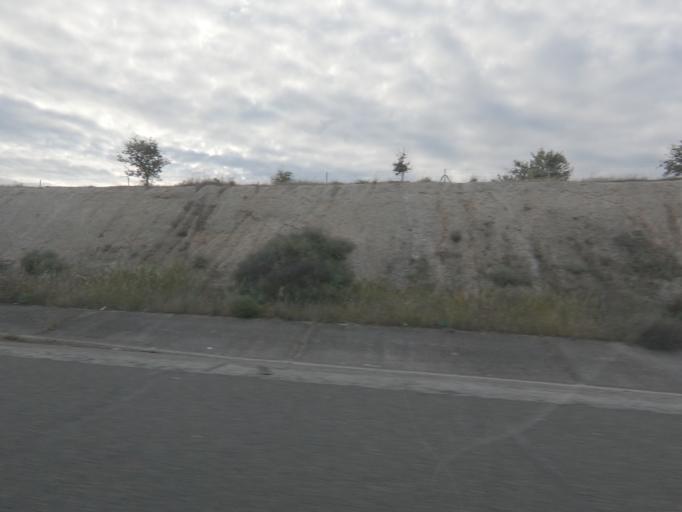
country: ES
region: Extremadura
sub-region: Provincia de Caceres
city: Casar de Caceres
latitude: 39.5071
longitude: -6.4357
